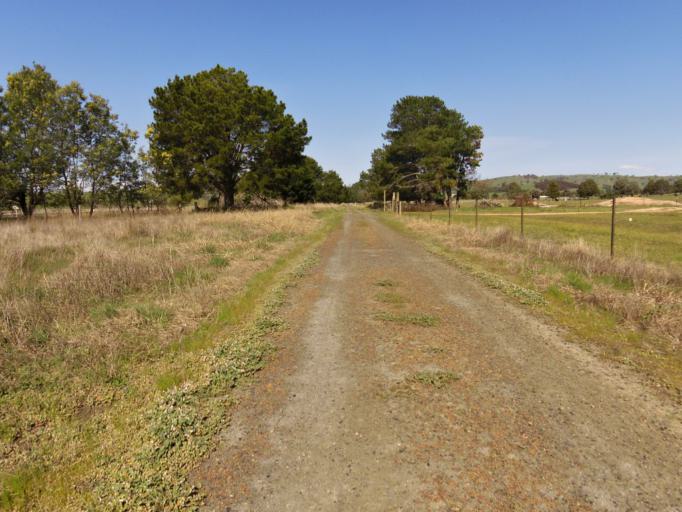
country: AU
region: Victoria
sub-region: Murrindindi
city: Alexandra
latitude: -37.0034
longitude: 145.7478
